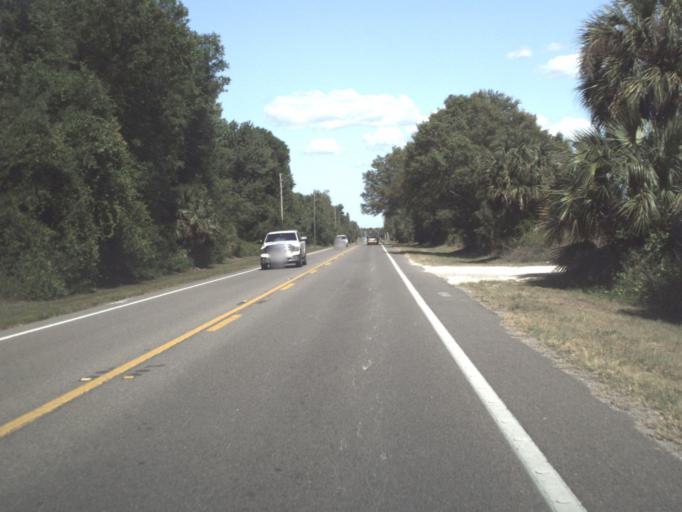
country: US
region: Florida
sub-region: Lake County
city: Mount Plymouth
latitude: 28.8127
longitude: -81.5145
